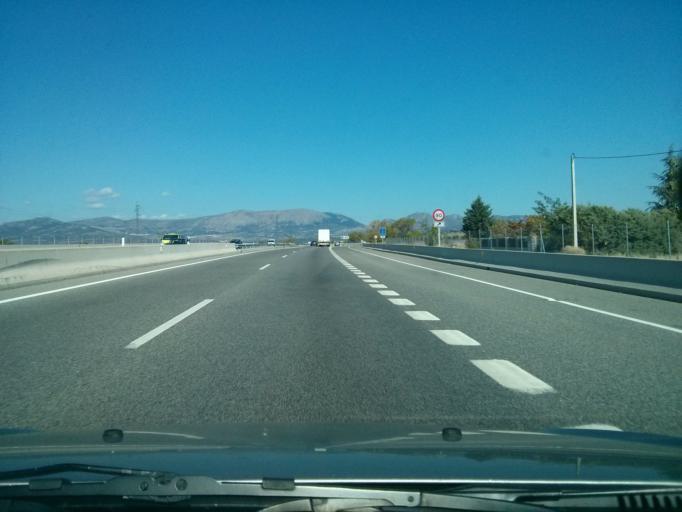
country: ES
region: Madrid
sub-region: Provincia de Madrid
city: Pedrezuela
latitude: 40.7610
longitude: -3.6020
